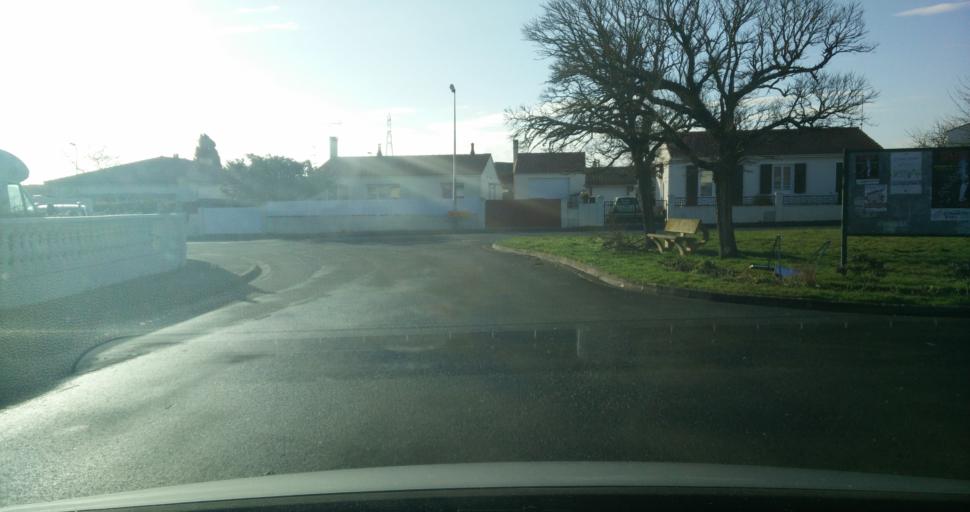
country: FR
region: Poitou-Charentes
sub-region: Departement de la Charente-Maritime
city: Saint-Xandre
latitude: 46.2035
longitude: -1.0964
